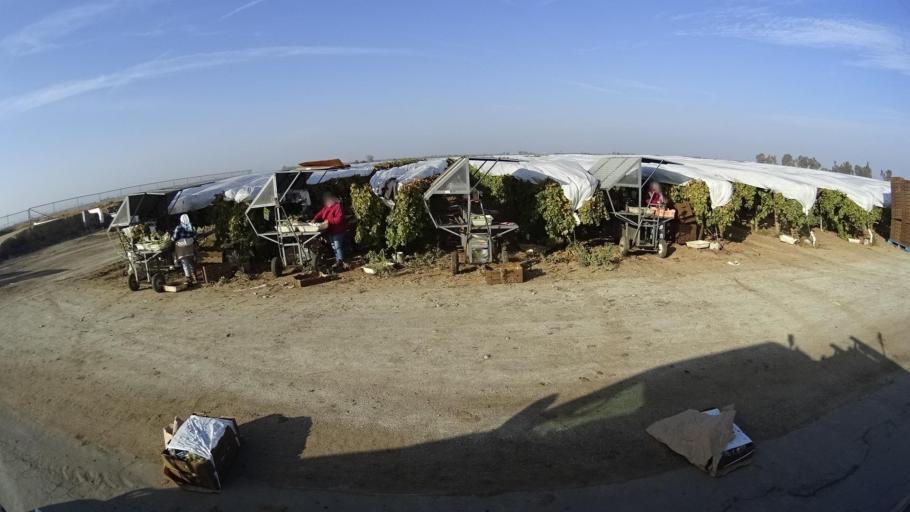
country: US
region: California
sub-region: Kern County
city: McFarland
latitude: 35.6836
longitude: -119.1870
